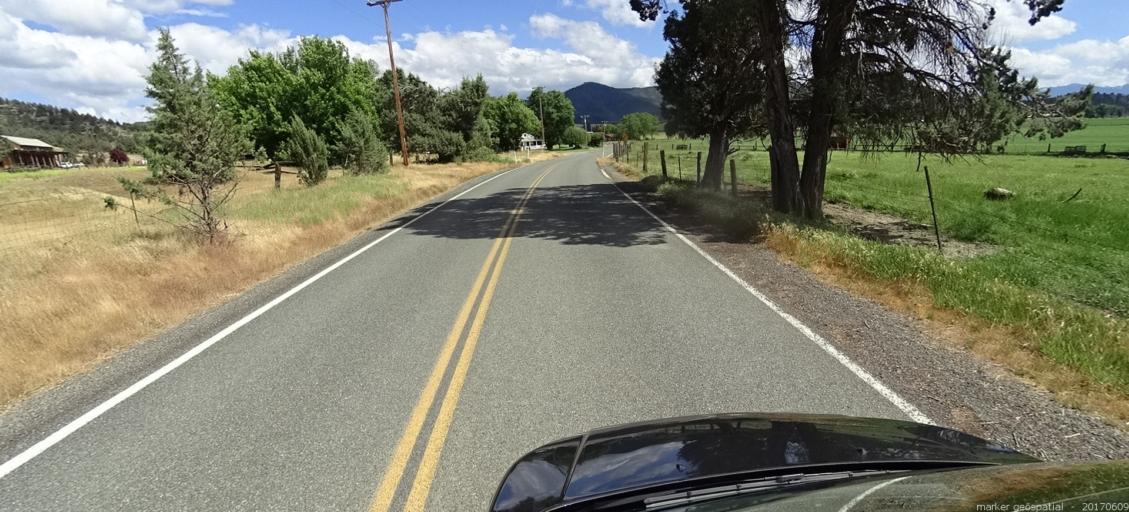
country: US
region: California
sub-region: Siskiyou County
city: Yreka
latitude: 41.5070
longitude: -122.8378
